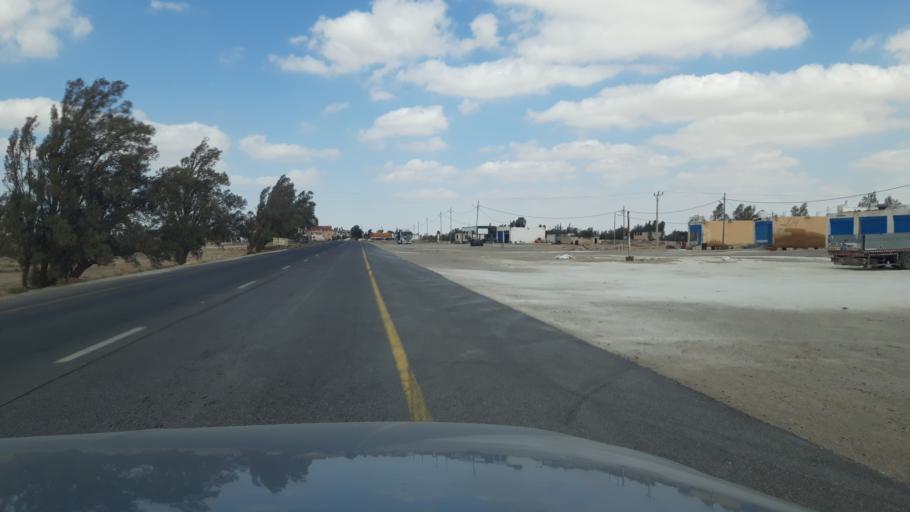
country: JO
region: Amman
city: Al Azraq ash Shamali
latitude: 31.8240
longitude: 36.8117
